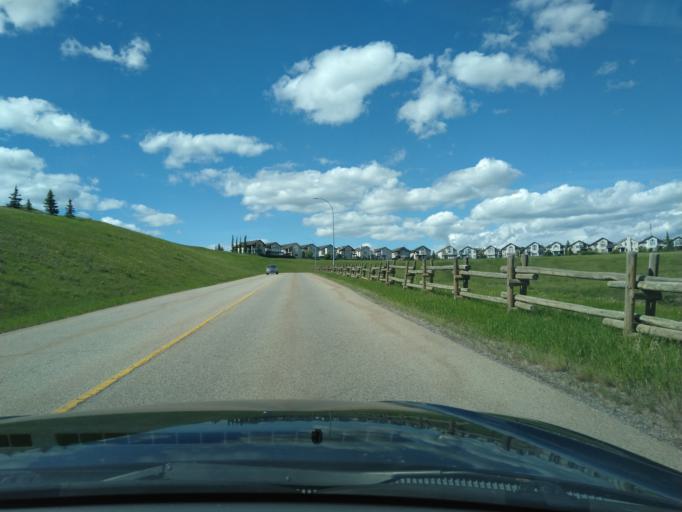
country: CA
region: Alberta
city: Cochrane
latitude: 51.1925
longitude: -114.4269
